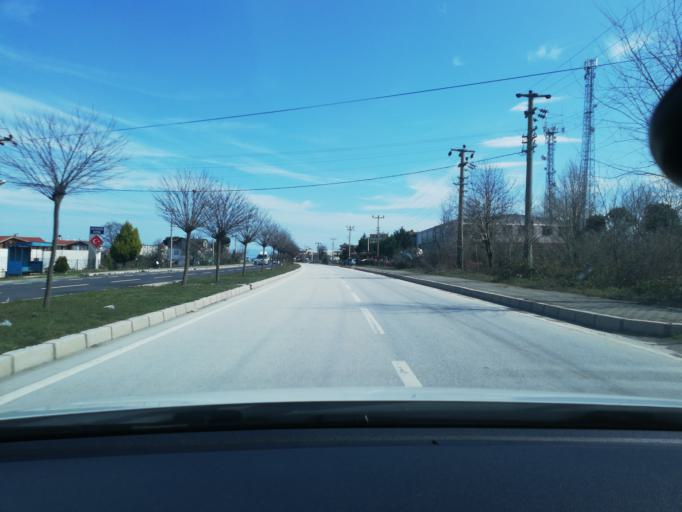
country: TR
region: Duzce
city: Akcakoca
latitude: 41.0884
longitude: 31.1825
